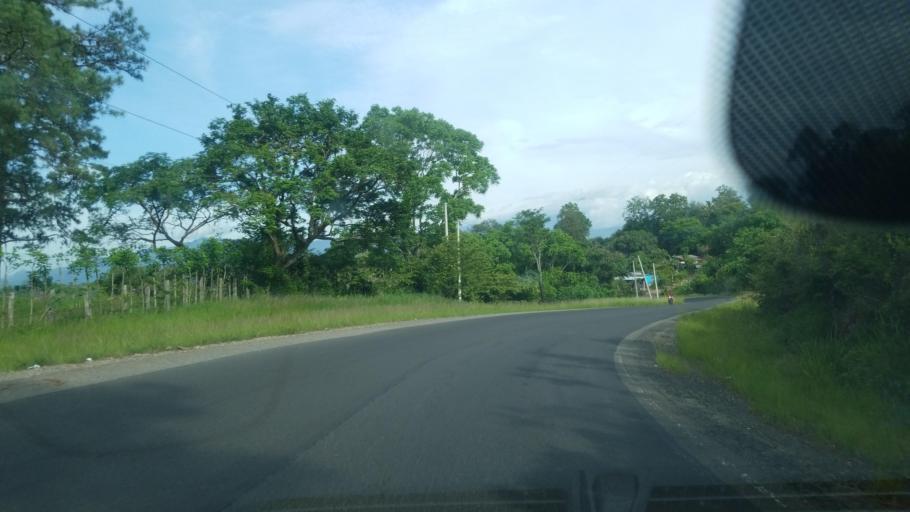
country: HN
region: Santa Barbara
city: Trinidad
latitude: 15.1721
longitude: -88.2644
